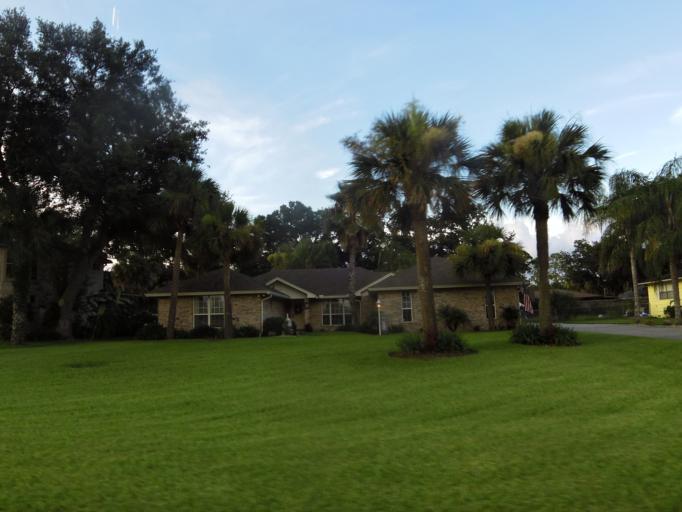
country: US
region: Florida
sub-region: Duval County
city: Atlantic Beach
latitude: 30.3941
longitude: -81.5018
